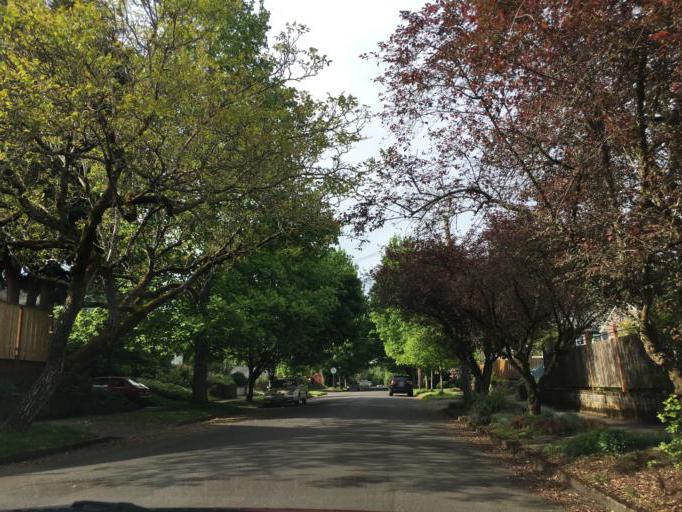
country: US
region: Oregon
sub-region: Multnomah County
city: Lents
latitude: 45.5034
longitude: -122.6161
